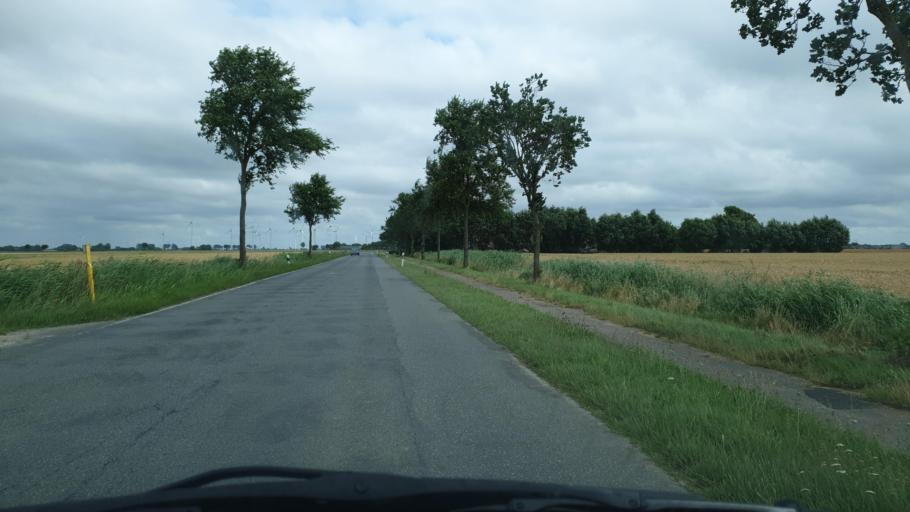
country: DE
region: Schleswig-Holstein
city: Friedrichskoog
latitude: 54.0217
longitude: 8.8755
